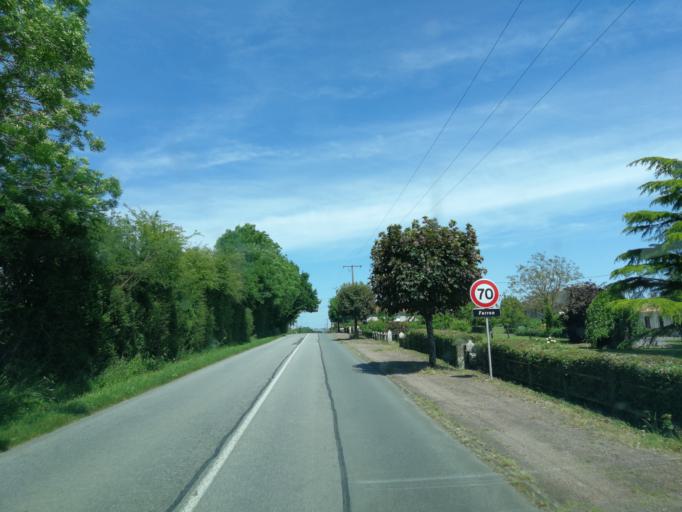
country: FR
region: Poitou-Charentes
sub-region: Departement des Deux-Sevres
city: Courlay
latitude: 46.8045
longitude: -0.5740
